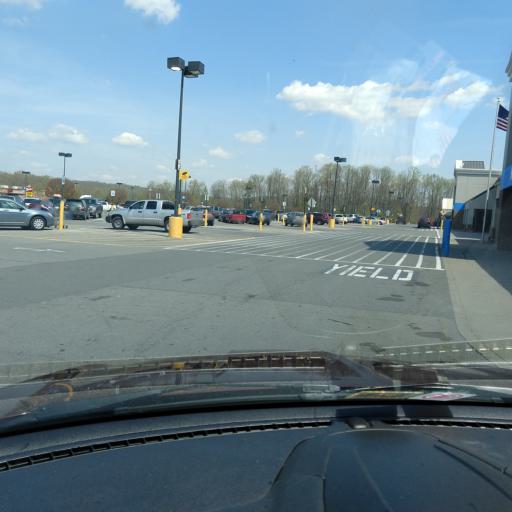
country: US
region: West Virginia
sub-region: Fayette County
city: Fayetteville
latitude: 38.0338
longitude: -81.1204
